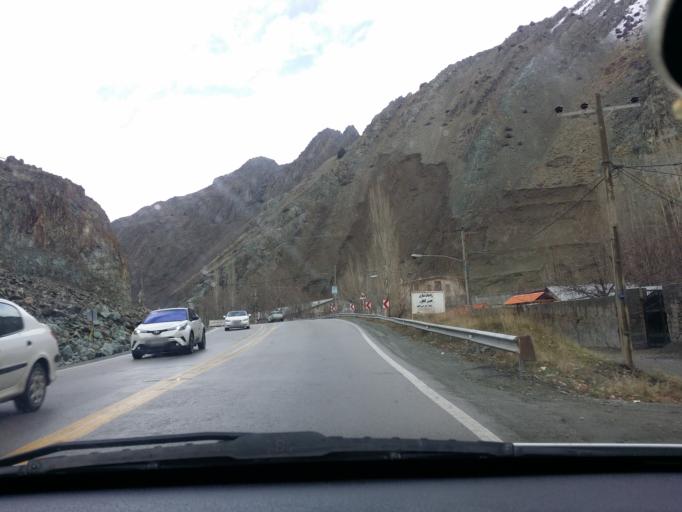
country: IR
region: Tehran
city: Tajrish
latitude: 36.0182
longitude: 51.3002
